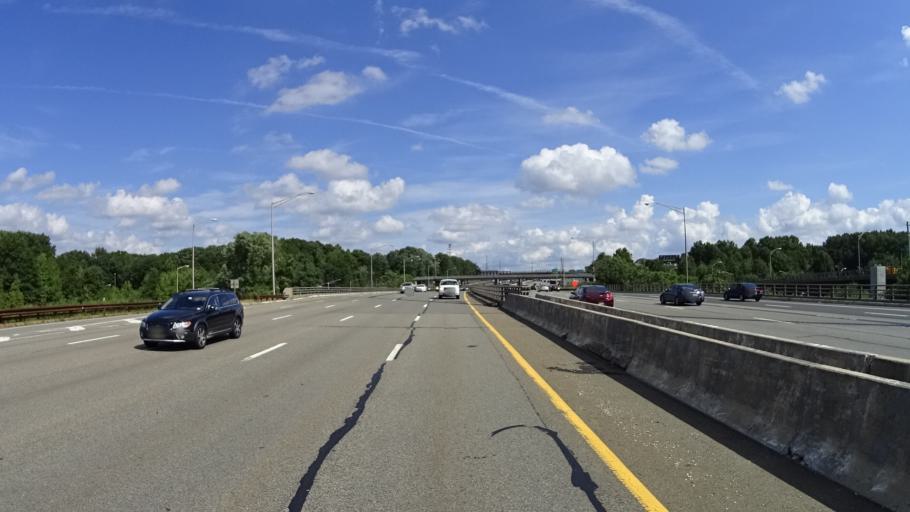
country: US
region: New Jersey
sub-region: Middlesex County
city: Fords
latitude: 40.5199
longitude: -74.3011
